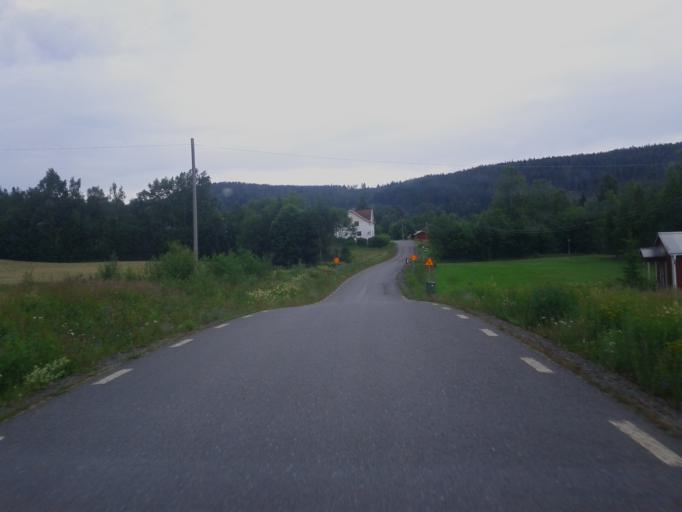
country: SE
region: Vaesternorrland
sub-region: Kramfors Kommun
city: Nordingra
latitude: 63.0636
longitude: 18.4127
